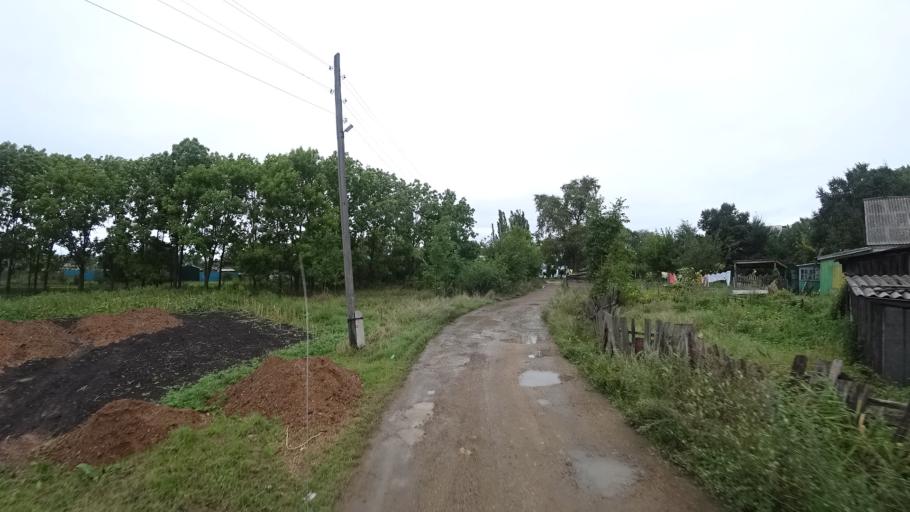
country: RU
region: Primorskiy
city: Chernigovka
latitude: 44.3382
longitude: 132.5440
